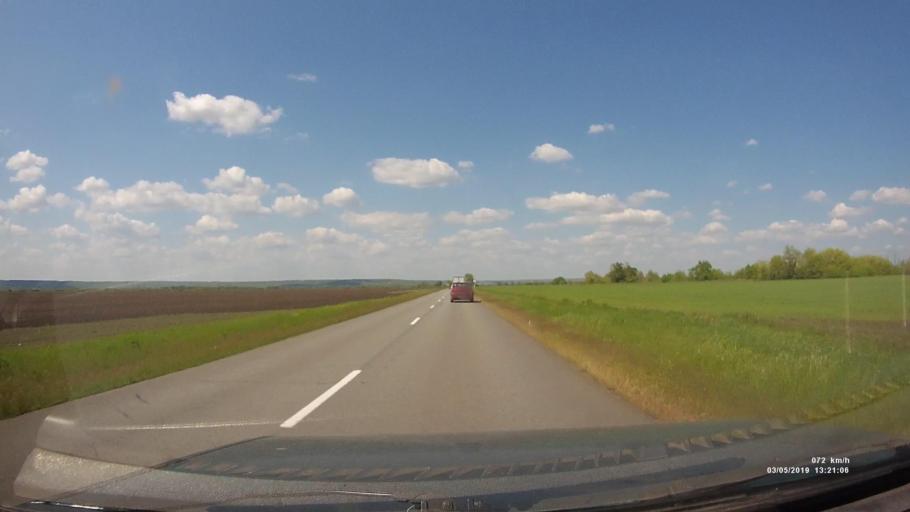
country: RU
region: Rostov
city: Semikarakorsk
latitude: 47.5520
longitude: 40.7491
